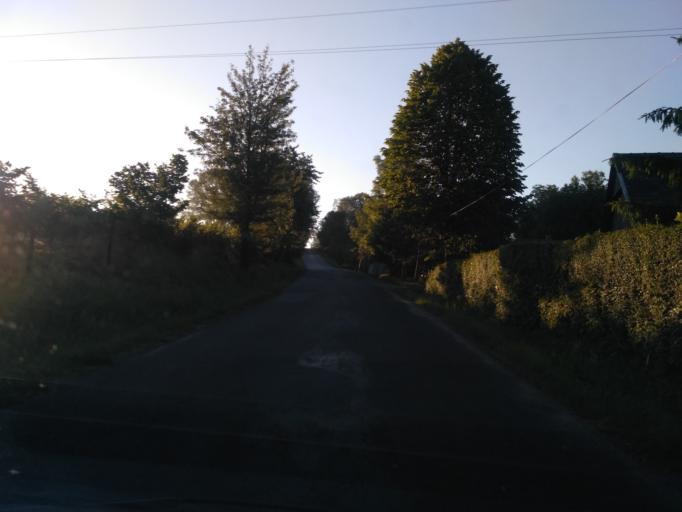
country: PL
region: Subcarpathian Voivodeship
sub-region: Powiat strzyzowski
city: Czudec
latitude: 49.8958
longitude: 21.8377
